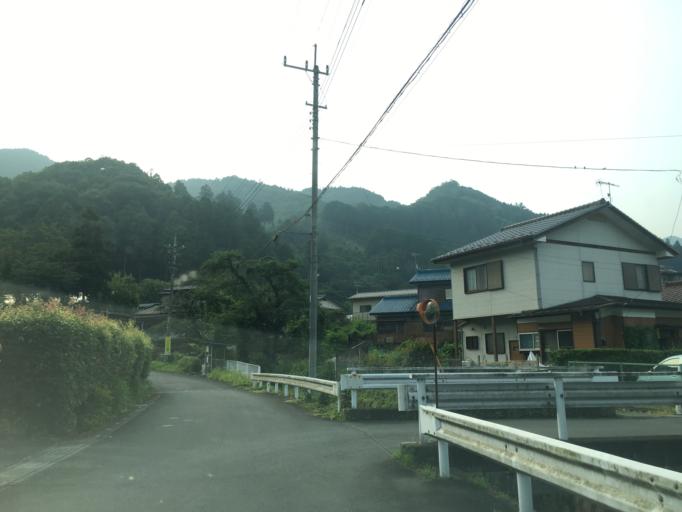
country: JP
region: Saitama
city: Chichibu
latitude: 35.9829
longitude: 139.1131
